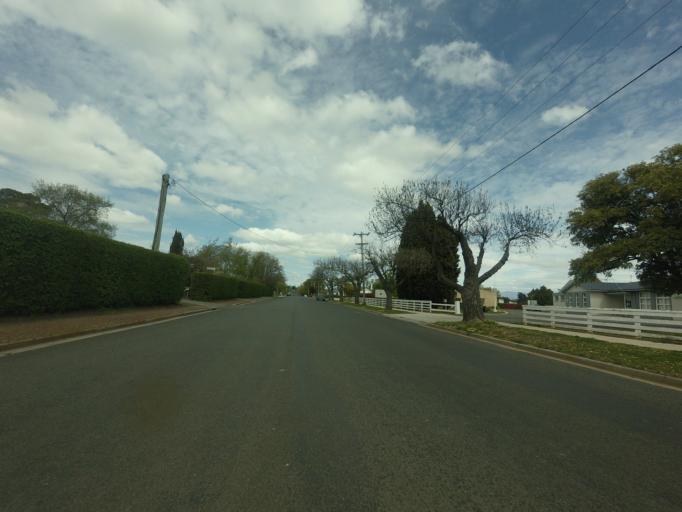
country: AU
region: Tasmania
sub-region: Northern Midlands
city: Longford
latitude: -41.5976
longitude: 147.1233
